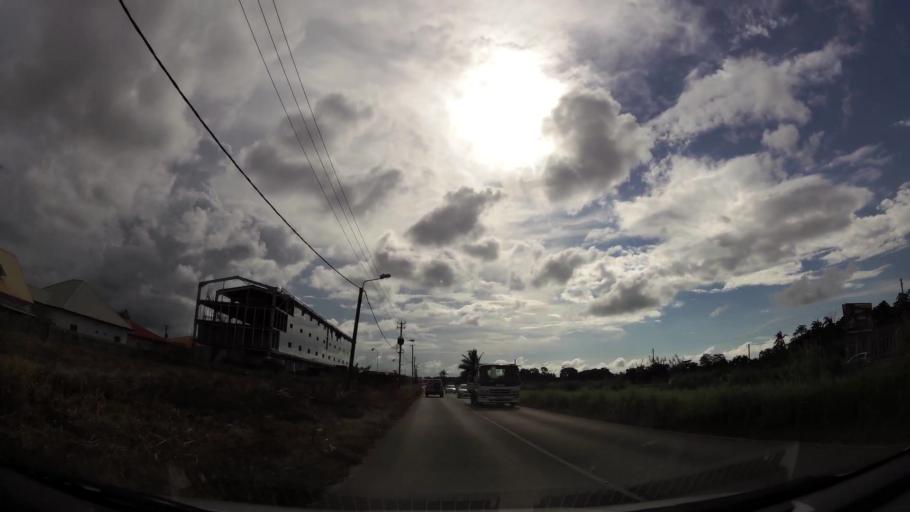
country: SR
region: Paramaribo
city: Paramaribo
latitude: 5.8561
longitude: -55.1619
